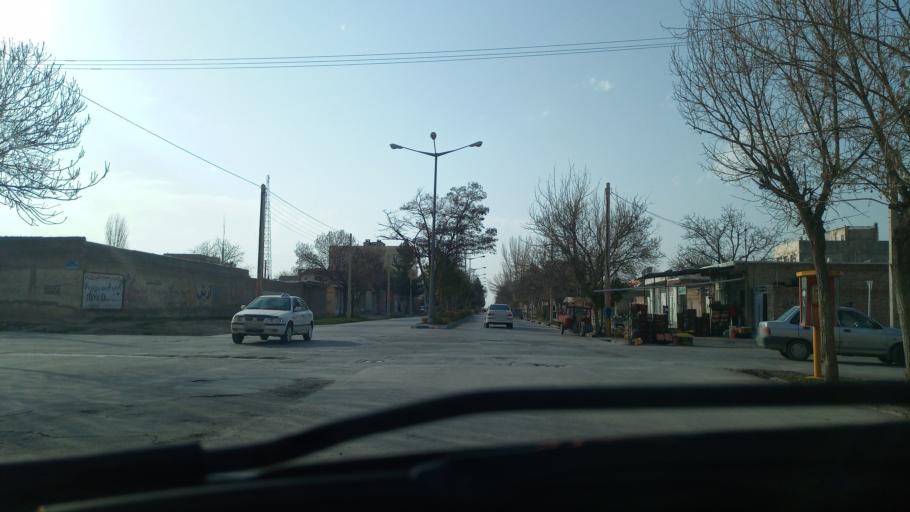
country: IR
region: Razavi Khorasan
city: Quchan
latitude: 37.1003
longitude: 58.5003
